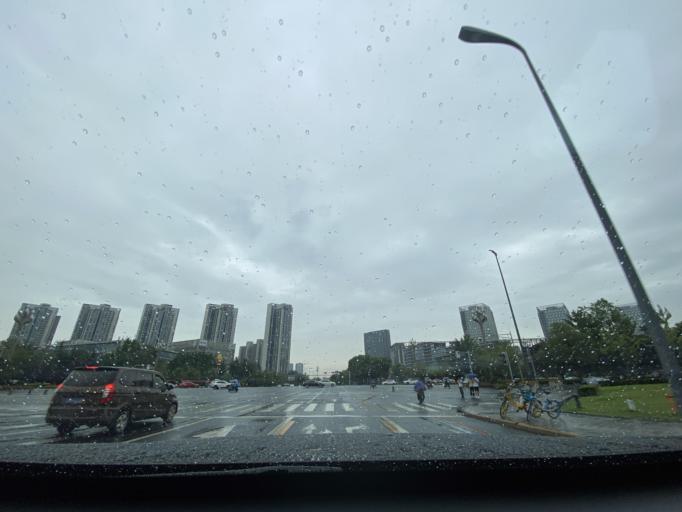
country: CN
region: Sichuan
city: Chengdu
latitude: 30.5448
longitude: 104.0659
